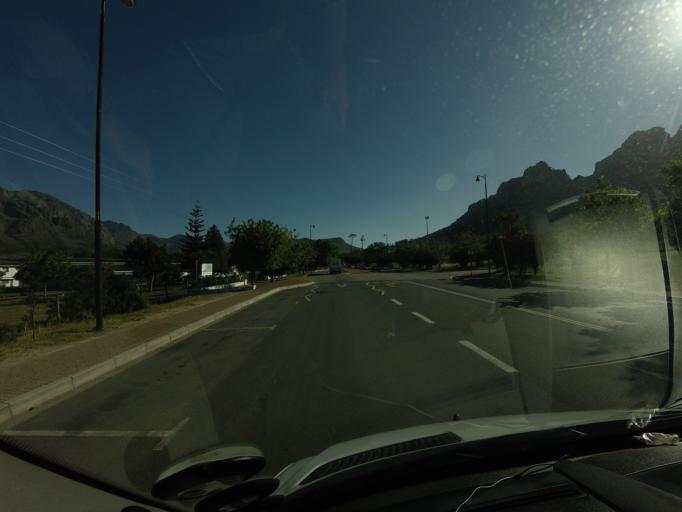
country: ZA
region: Western Cape
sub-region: Cape Winelands District Municipality
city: Stellenbosch
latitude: -33.8850
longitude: 18.9669
